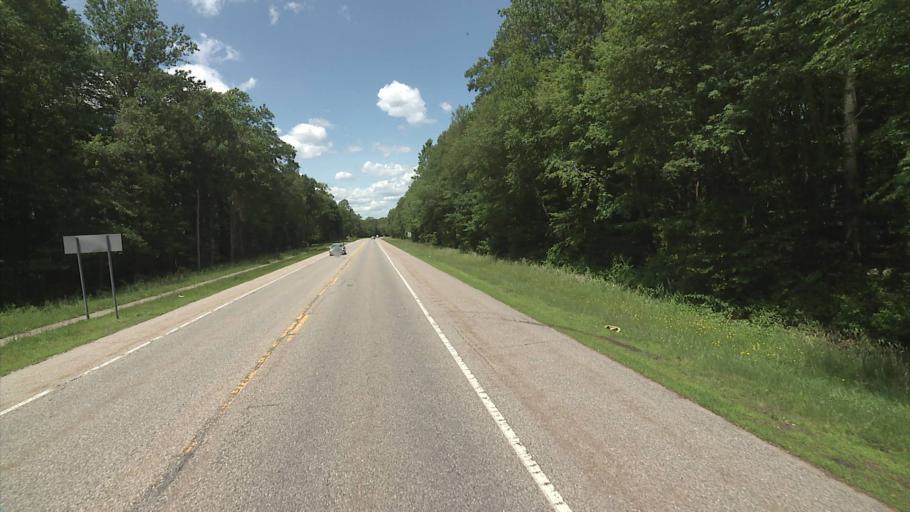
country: US
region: Connecticut
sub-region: New London County
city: Mystic
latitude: 41.3621
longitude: -71.9801
